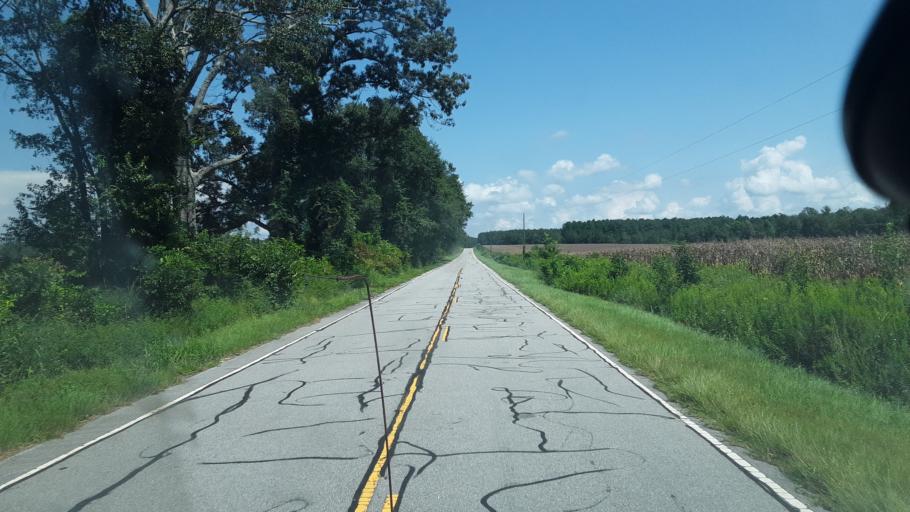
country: US
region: South Carolina
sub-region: Orangeburg County
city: Edisto
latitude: 33.5873
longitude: -81.0337
